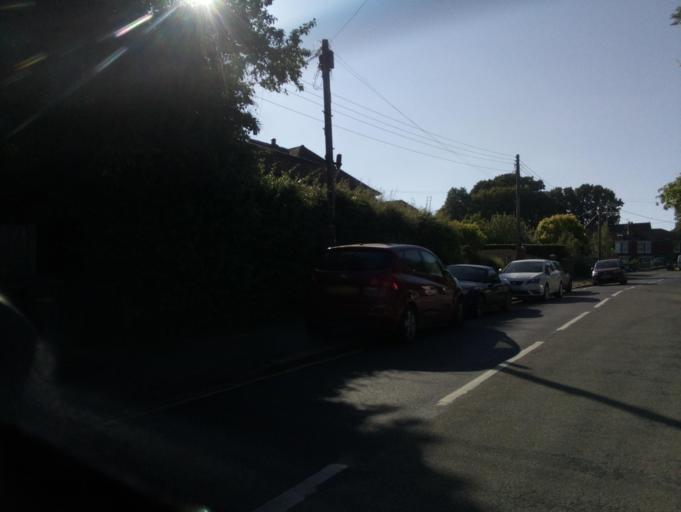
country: GB
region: England
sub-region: Hampshire
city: Eastleigh
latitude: 50.9890
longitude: -1.3461
